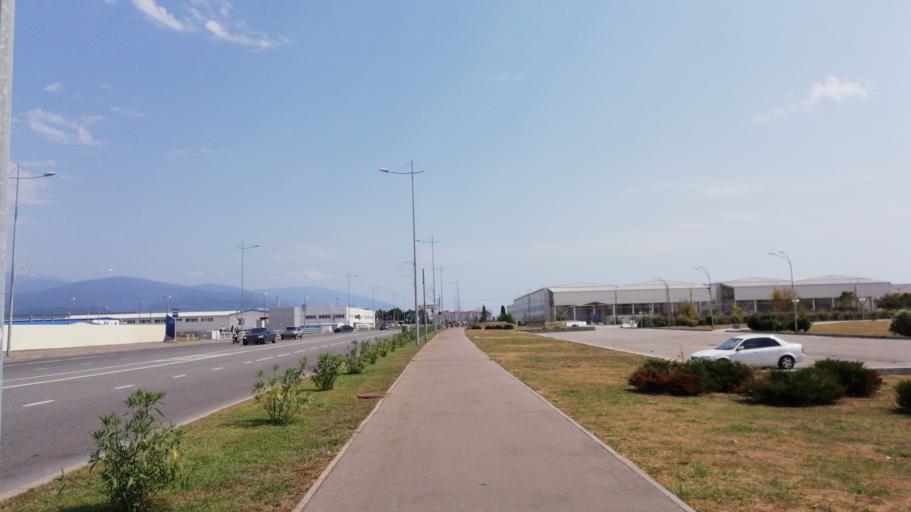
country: RU
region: Krasnodarskiy
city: Adler
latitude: 43.3988
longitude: 39.9818
